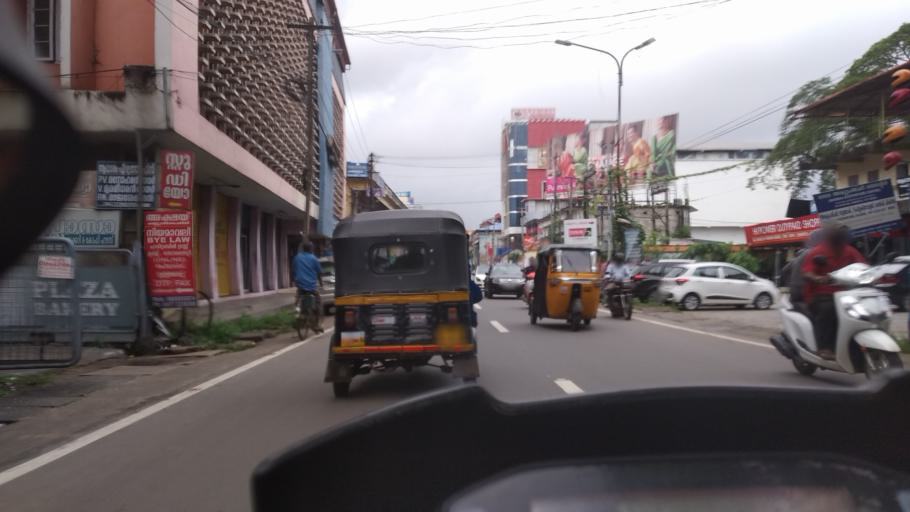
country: IN
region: Kerala
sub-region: Alappuzha
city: Alleppey
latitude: 9.4936
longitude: 76.3387
